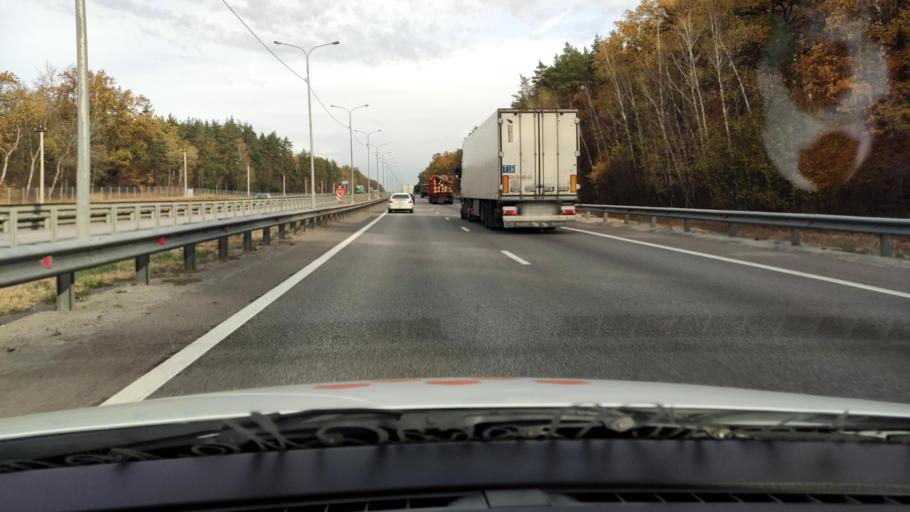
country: RU
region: Voronezj
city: Ramon'
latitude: 51.8706
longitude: 39.2165
